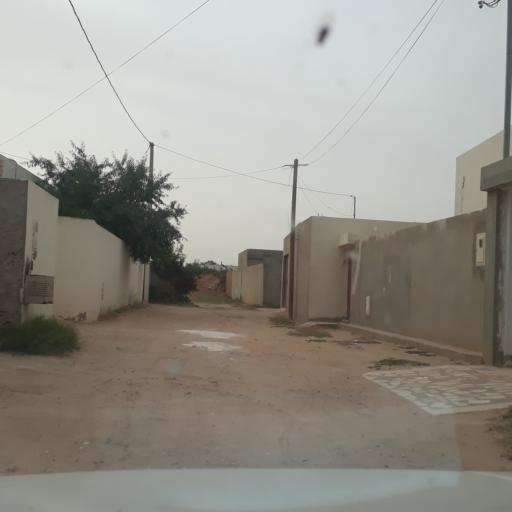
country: TN
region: Safaqis
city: Al Qarmadah
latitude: 34.8208
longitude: 10.7710
